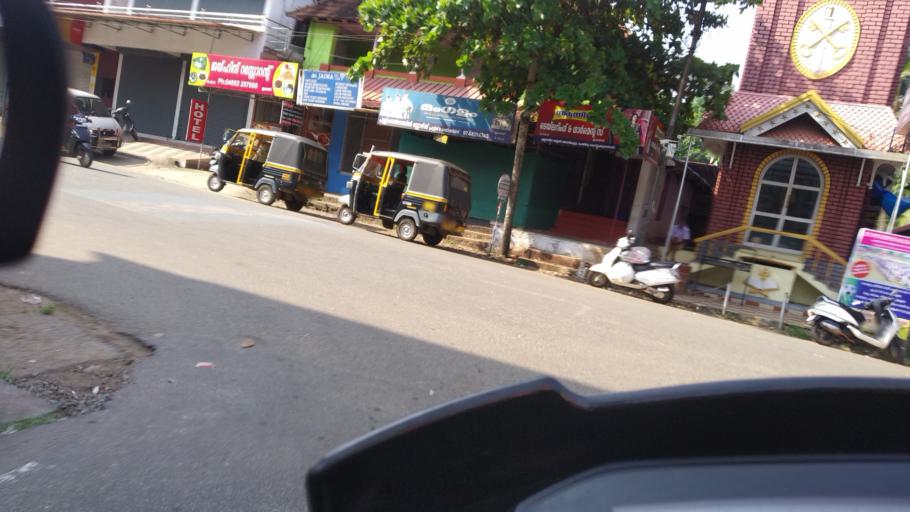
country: IN
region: Kerala
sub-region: Ernakulam
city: Piravam
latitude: 9.8307
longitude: 76.5452
